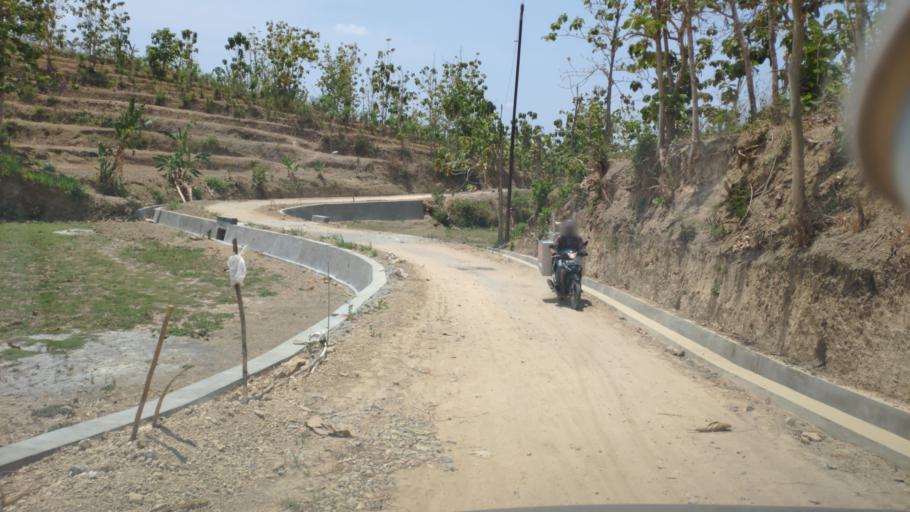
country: ID
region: Central Java
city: Singonegoro
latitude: -6.9719
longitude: 111.5245
